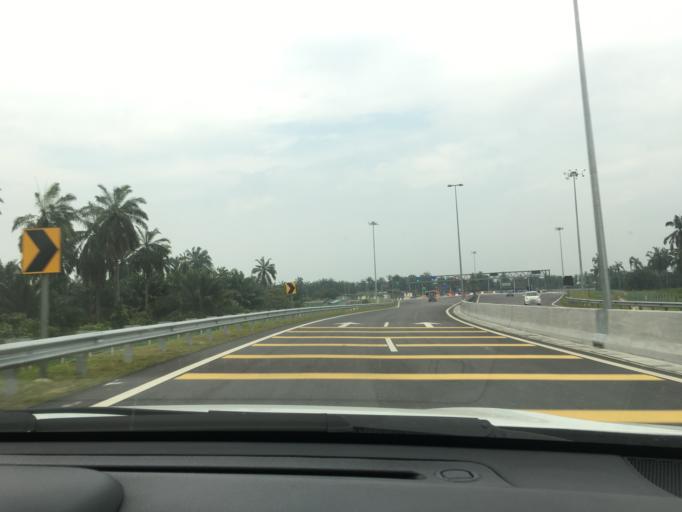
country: MY
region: Selangor
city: Klang
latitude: 3.1284
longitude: 101.3994
